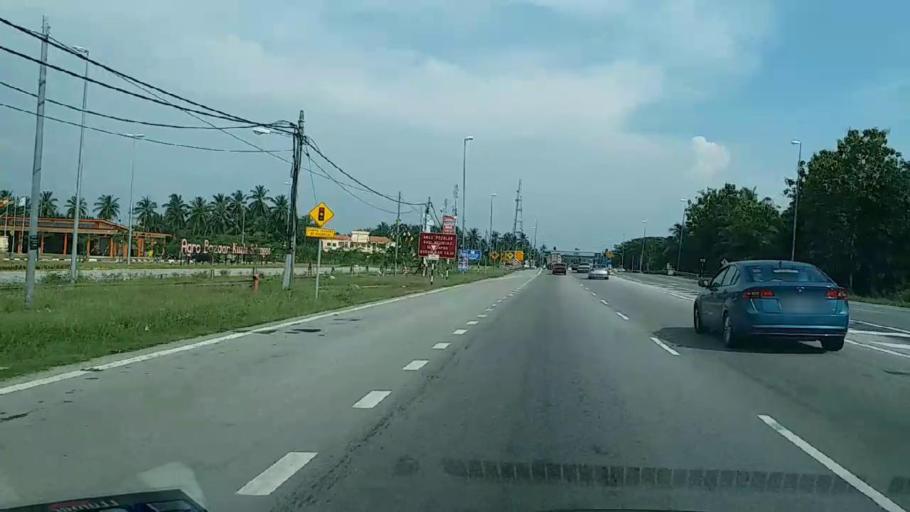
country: MY
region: Selangor
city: Kuala Selangor
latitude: 3.3650
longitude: 101.2456
